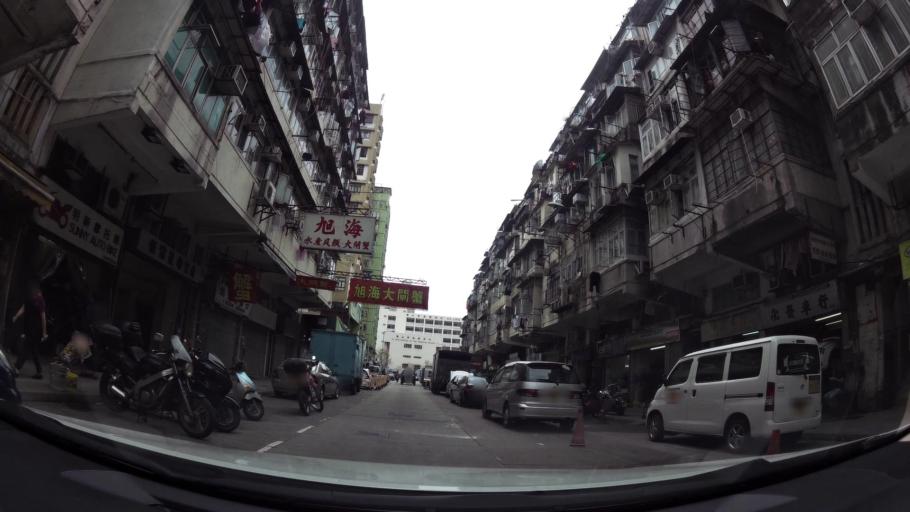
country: HK
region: Sham Shui Po
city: Sham Shui Po
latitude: 22.3288
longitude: 114.1577
